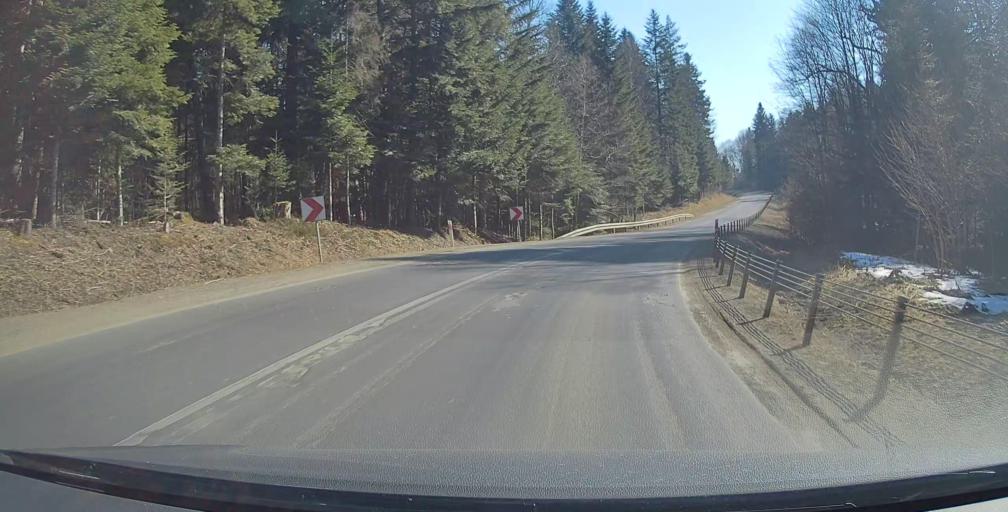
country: PL
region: Subcarpathian Voivodeship
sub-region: Powiat bieszczadzki
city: Ustrzyki Dolne
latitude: 49.5207
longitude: 22.6045
